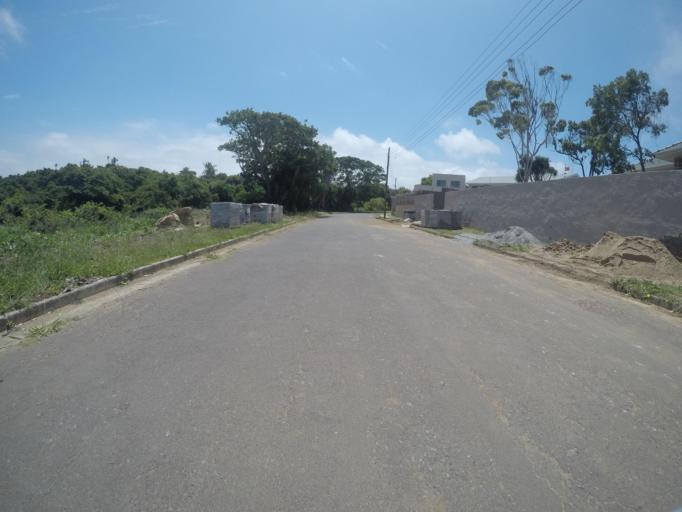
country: ZA
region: Eastern Cape
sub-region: Buffalo City Metropolitan Municipality
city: East London
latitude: -33.0039
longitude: 27.9185
